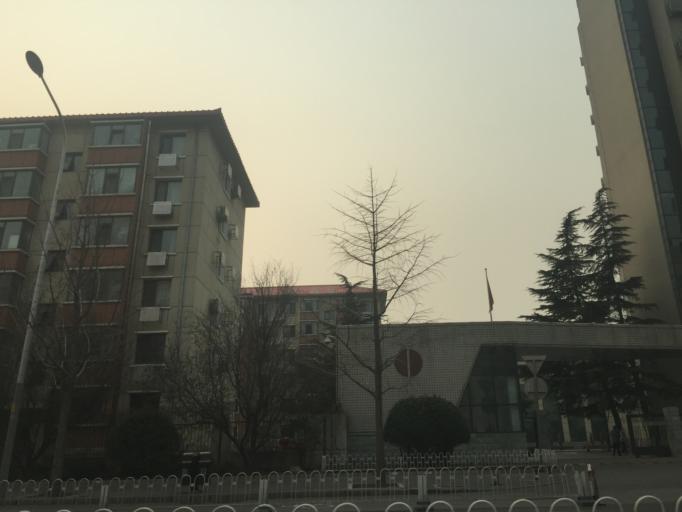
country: CN
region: Beijing
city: Datun
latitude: 39.9812
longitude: 116.3831
